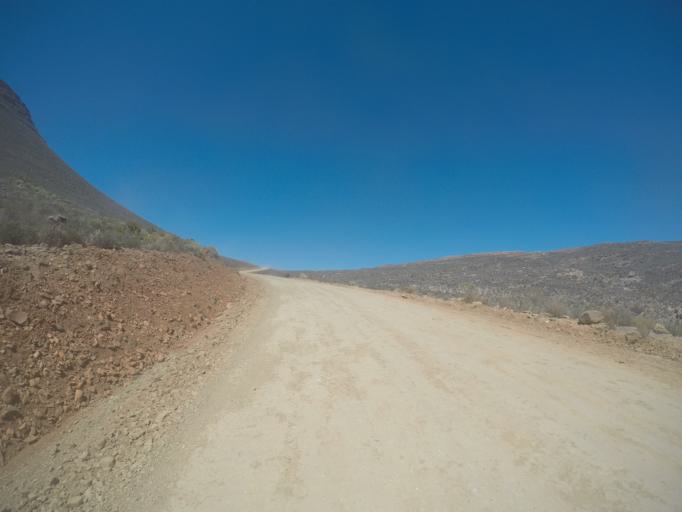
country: ZA
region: Western Cape
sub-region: West Coast District Municipality
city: Clanwilliam
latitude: -32.6066
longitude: 19.3677
